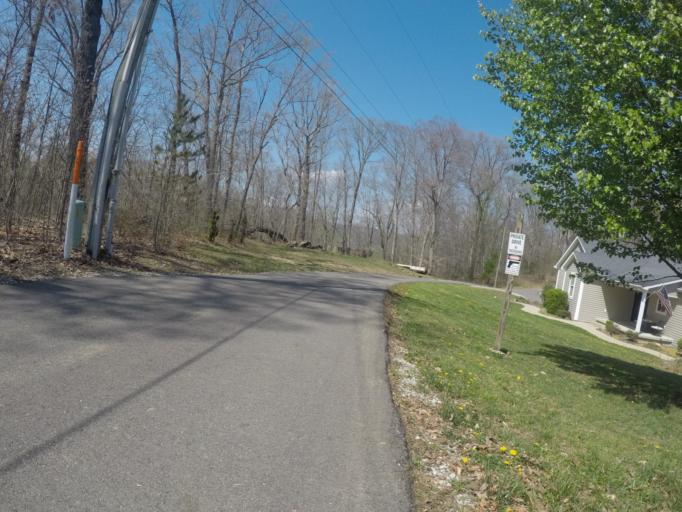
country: US
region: Ohio
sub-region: Lawrence County
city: Burlington
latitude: 38.3918
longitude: -82.5353
